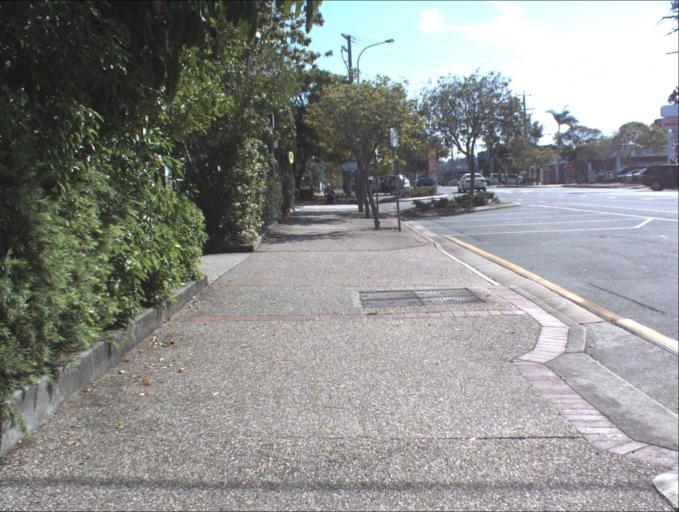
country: AU
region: Queensland
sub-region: Logan
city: Beenleigh
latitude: -27.7172
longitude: 153.2007
